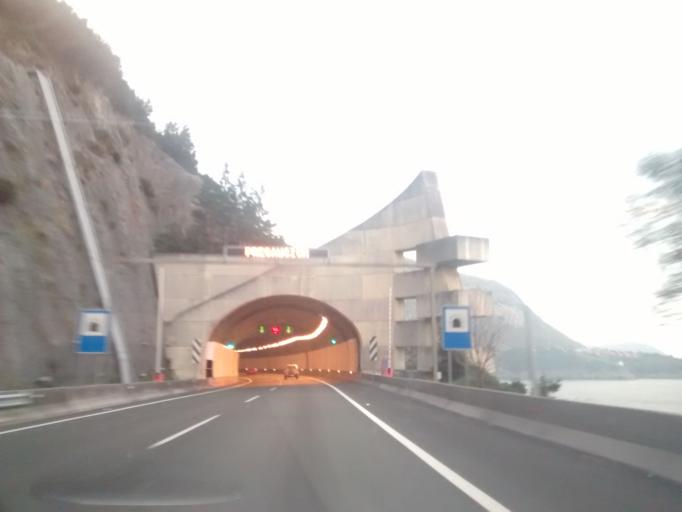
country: ES
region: Cantabria
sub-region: Provincia de Cantabria
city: Liendo
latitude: 43.4025
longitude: -3.3083
